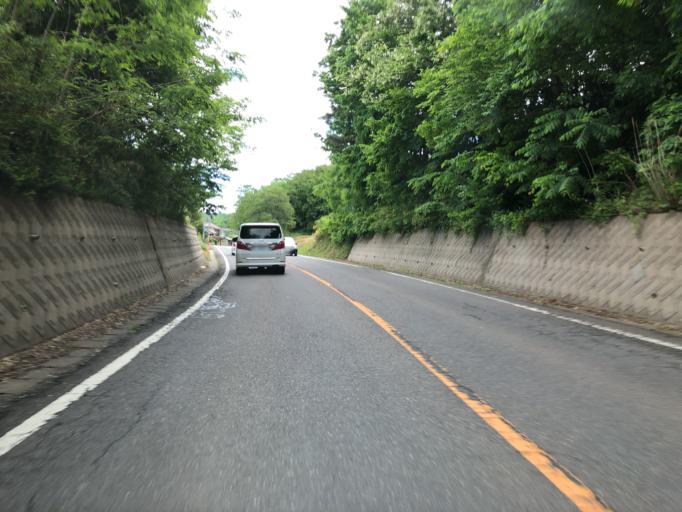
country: JP
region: Fukushima
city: Motomiya
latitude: 37.5117
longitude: 140.4231
